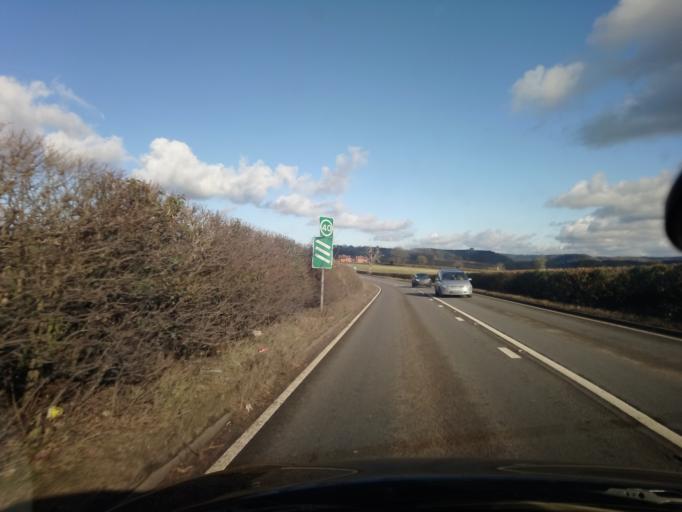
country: GB
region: England
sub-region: Shropshire
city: Clive
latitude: 52.8130
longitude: -2.6885
